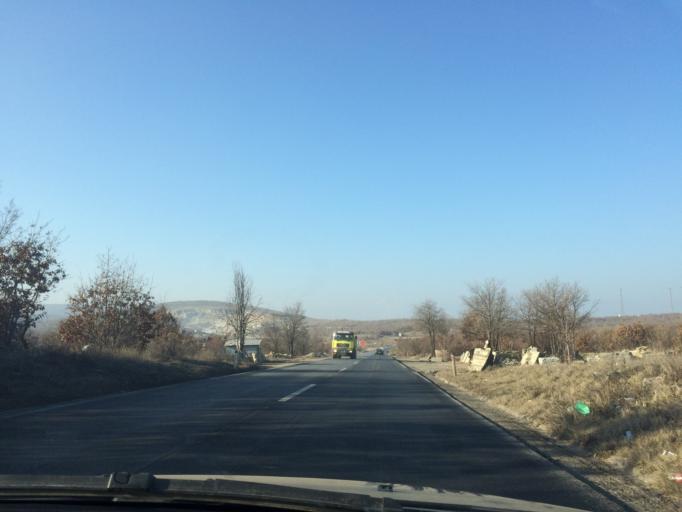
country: XK
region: Pec
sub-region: Komuna e Klines
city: Klina
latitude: 42.5944
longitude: 20.6406
